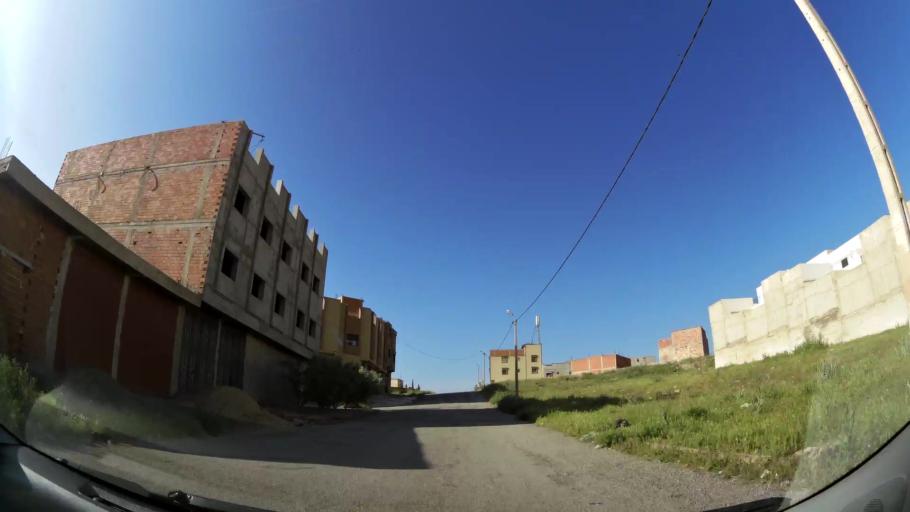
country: MA
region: Oriental
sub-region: Oujda-Angad
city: Oujda
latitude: 34.6735
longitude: -1.9452
